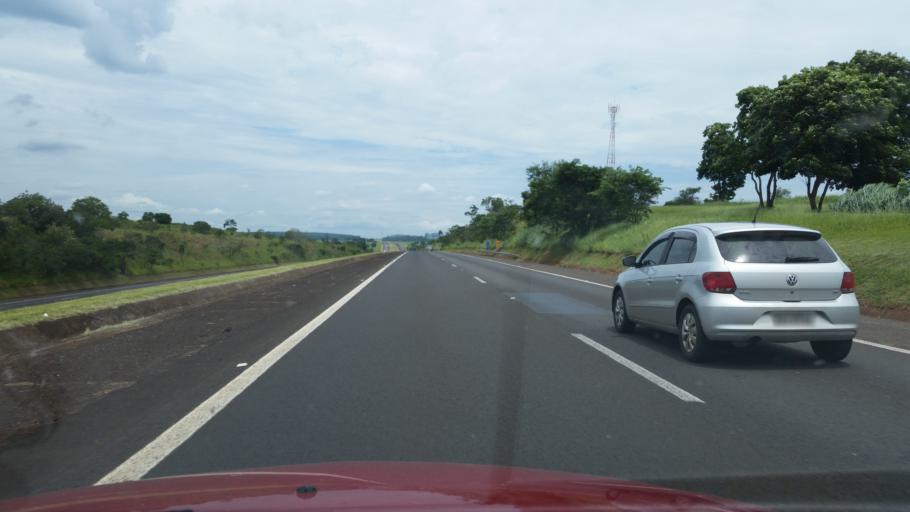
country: BR
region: Sao Paulo
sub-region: Avare
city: Avare
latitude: -22.9784
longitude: -48.7814
